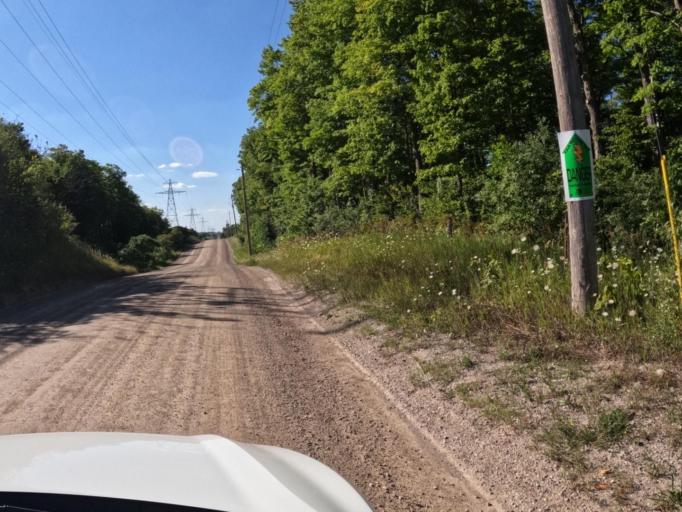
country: CA
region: Ontario
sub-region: Wellington County
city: Guelph
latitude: 43.4361
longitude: -80.1374
